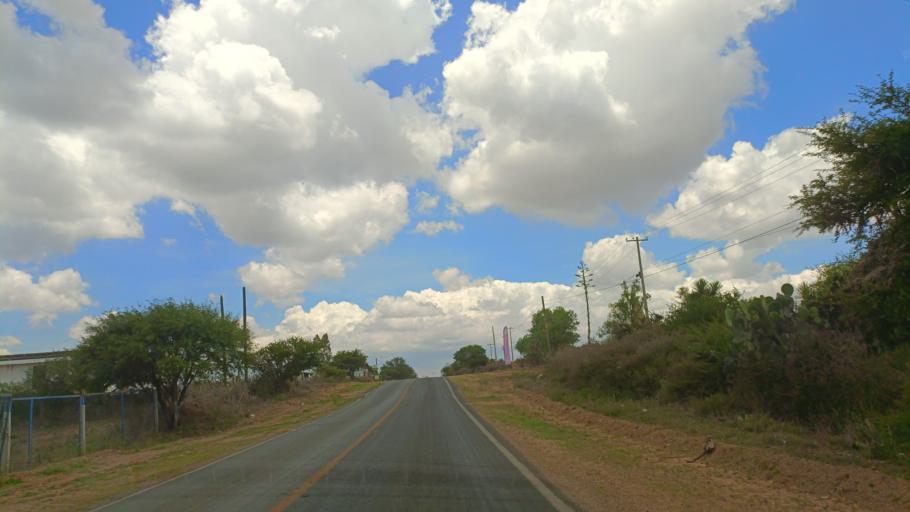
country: MX
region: Guanajuato
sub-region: San Luis de la Paz
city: San Ignacio
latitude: 21.2396
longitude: -100.4921
